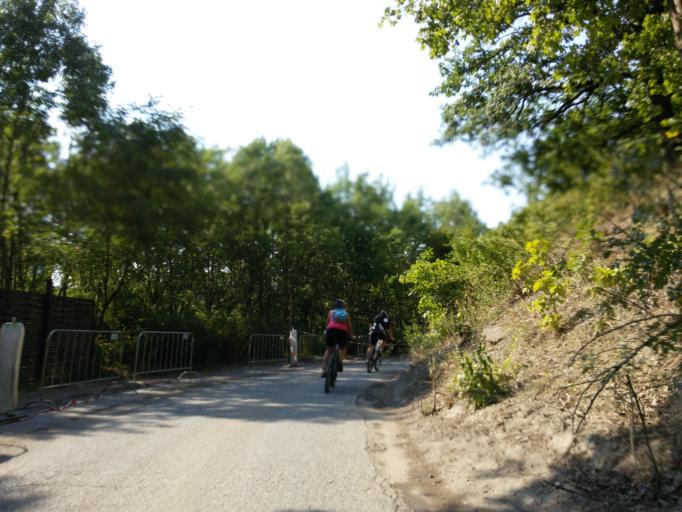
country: CZ
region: South Moravian
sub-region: Mesto Brno
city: Mokra Hora
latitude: 49.2376
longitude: 16.5923
